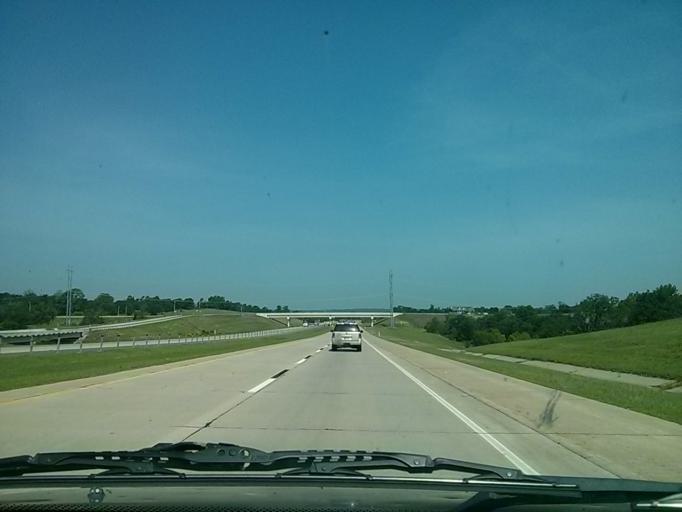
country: US
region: Oklahoma
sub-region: Creek County
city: Sapulpa
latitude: 36.0169
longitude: -96.0625
